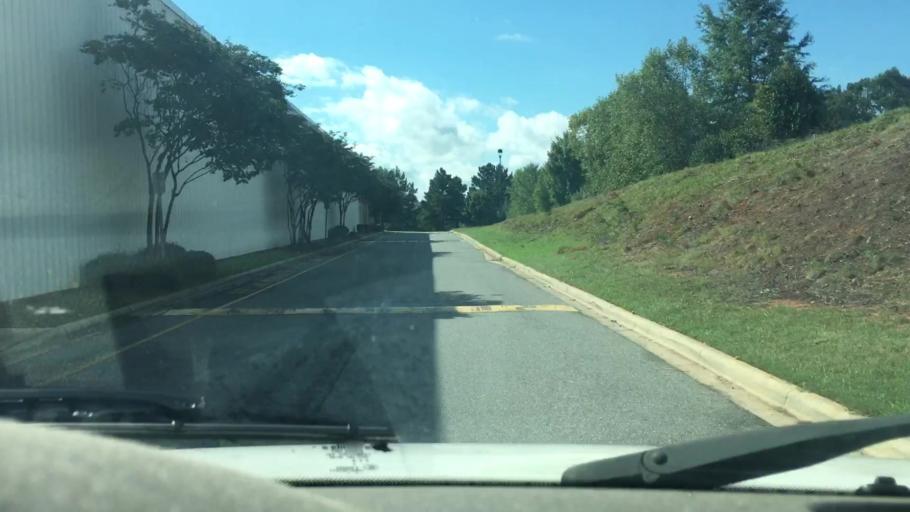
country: US
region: North Carolina
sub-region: Iredell County
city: Mooresville
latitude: 35.5996
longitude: -80.8624
